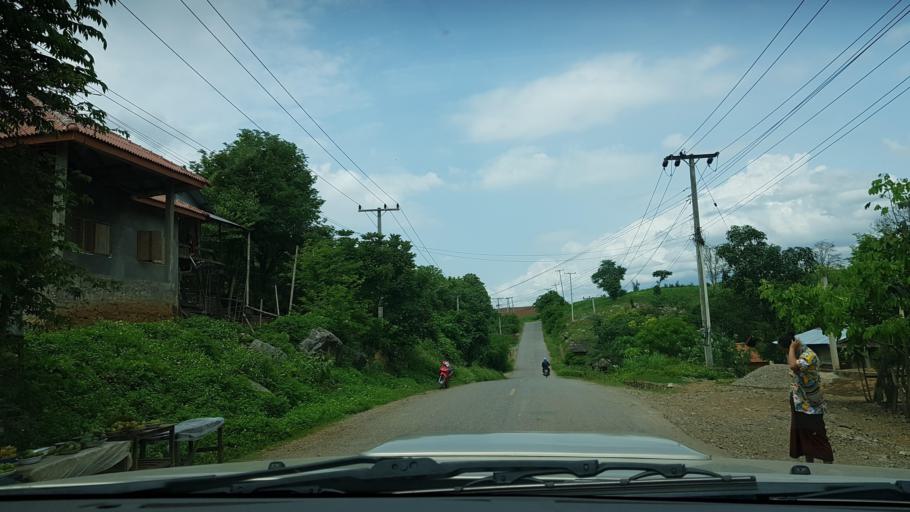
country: TH
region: Nan
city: Chaloem Phra Kiat
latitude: 20.0124
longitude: 101.3159
